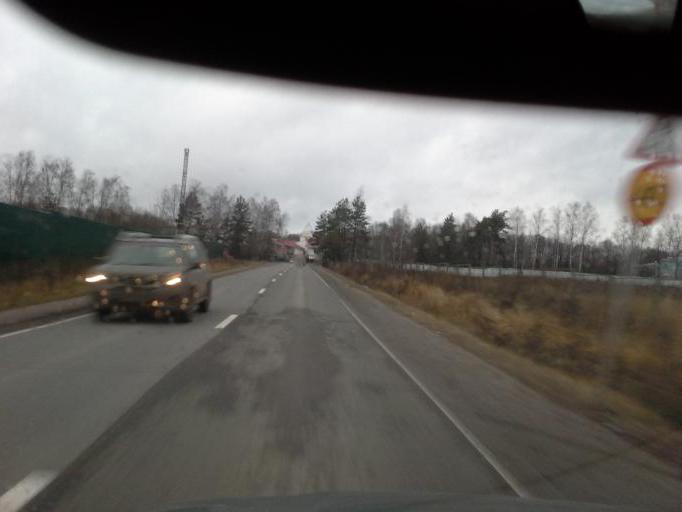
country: RU
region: Moskovskaya
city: Kokoshkino
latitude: 55.6164
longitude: 37.1587
